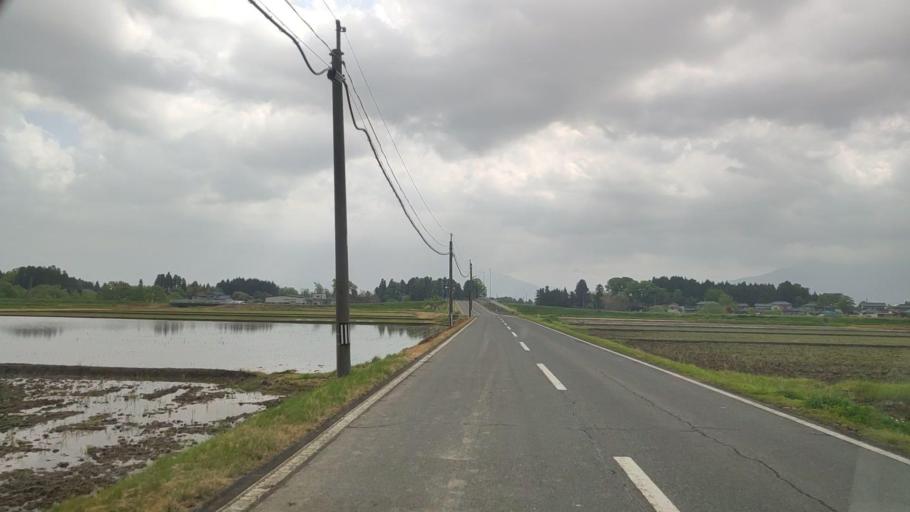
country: JP
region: Niigata
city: Gosen
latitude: 37.7281
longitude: 139.1500
